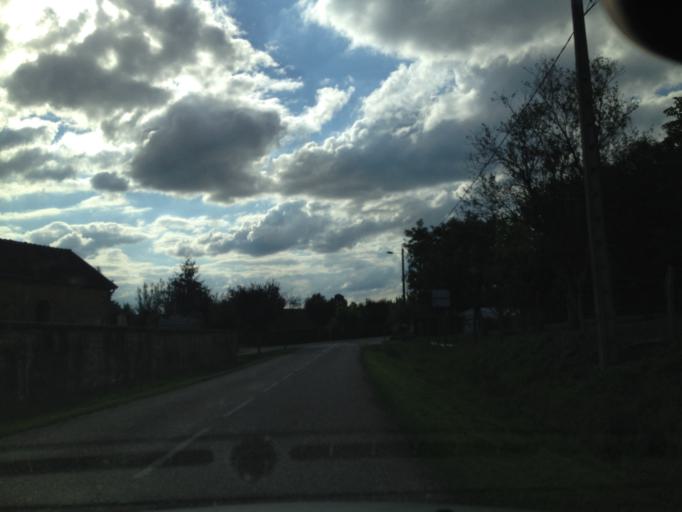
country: FR
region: Franche-Comte
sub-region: Departement de la Haute-Saone
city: Faverney
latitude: 47.7860
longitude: 6.0157
